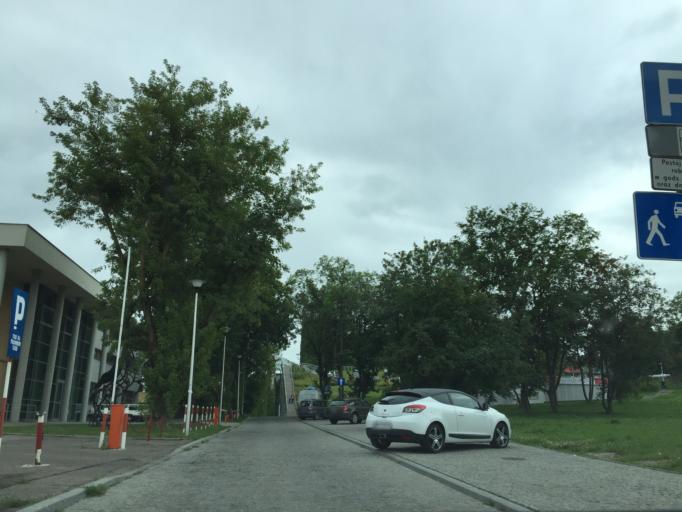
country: PL
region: Podlasie
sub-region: Bialystok
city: Bialystok
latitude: 53.1312
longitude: 23.1497
